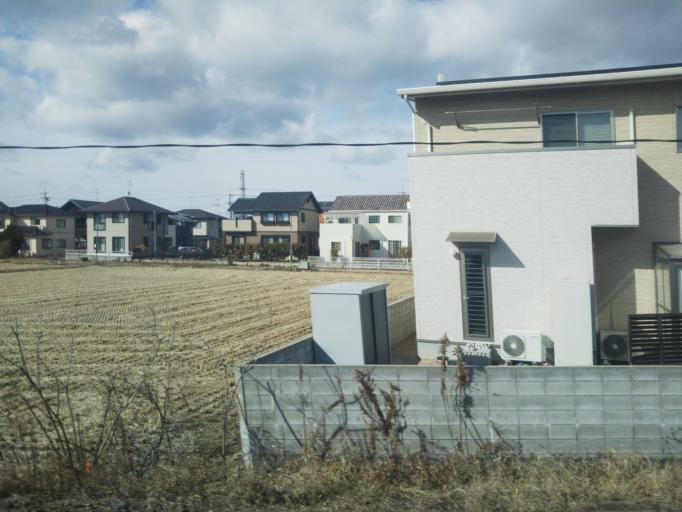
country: JP
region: Okayama
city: Okayama-shi
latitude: 34.6081
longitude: 133.8707
